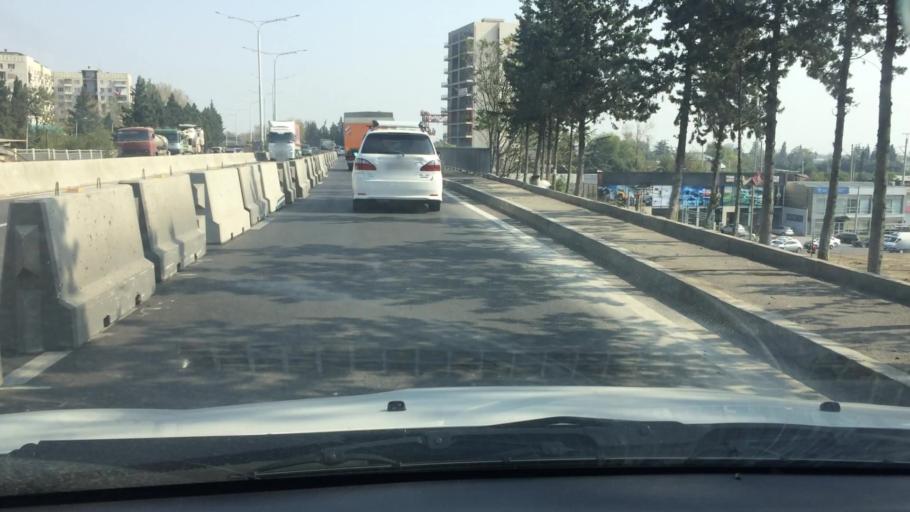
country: GE
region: T'bilisi
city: Tbilisi
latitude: 41.6843
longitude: 44.8694
